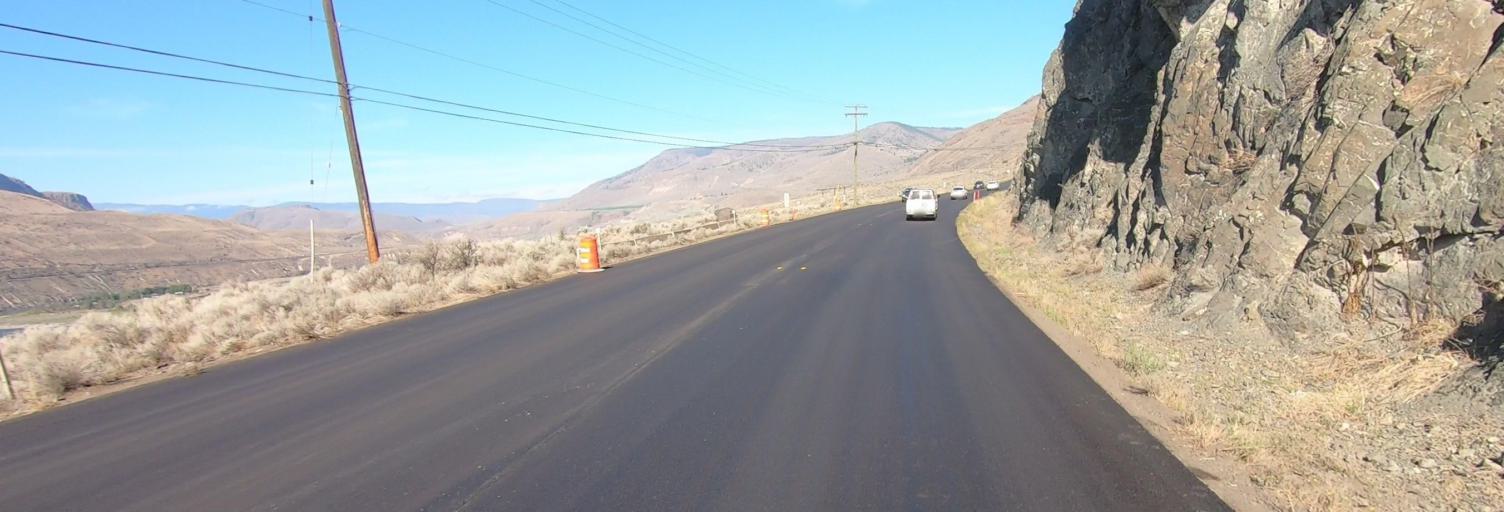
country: CA
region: British Columbia
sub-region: Thompson-Nicola Regional District
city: Ashcroft
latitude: 50.7825
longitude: -121.0609
